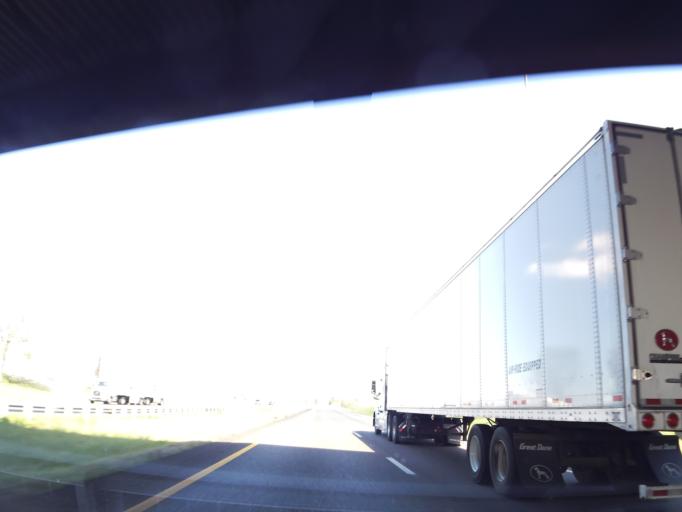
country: US
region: Tennessee
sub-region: Henderson County
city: Lexington
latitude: 35.7891
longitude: -88.3918
